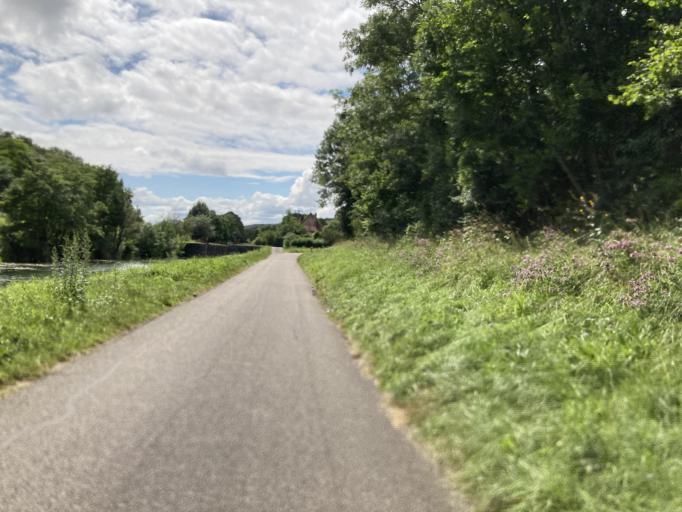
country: FR
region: Bourgogne
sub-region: Departement de la Cote-d'Or
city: Plombieres-les-Dijon
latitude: 47.3374
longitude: 4.9563
